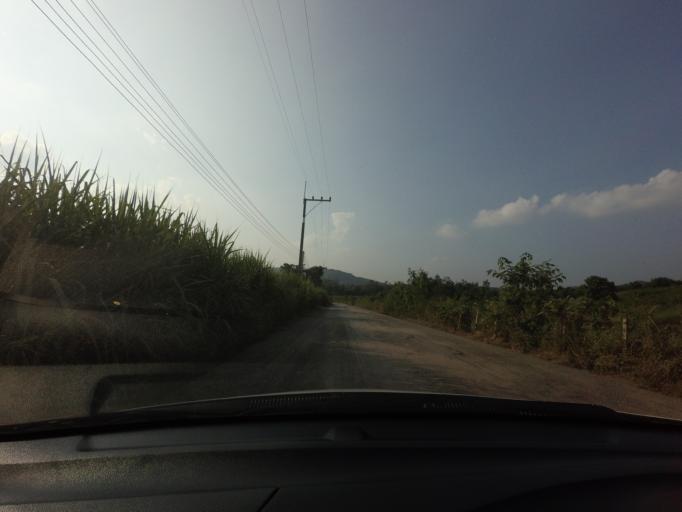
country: TH
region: Nakhon Ratchasima
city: Pak Chong
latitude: 14.5404
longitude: 101.5798
